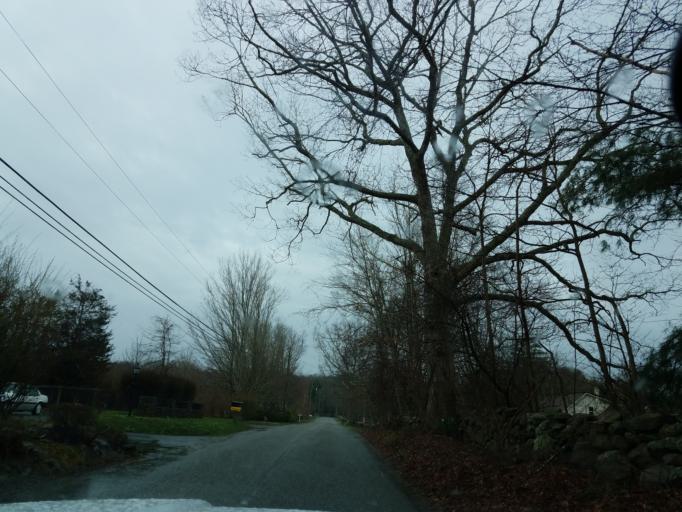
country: US
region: Rhode Island
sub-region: Washington County
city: Ashaway
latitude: 41.4500
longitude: -71.8224
